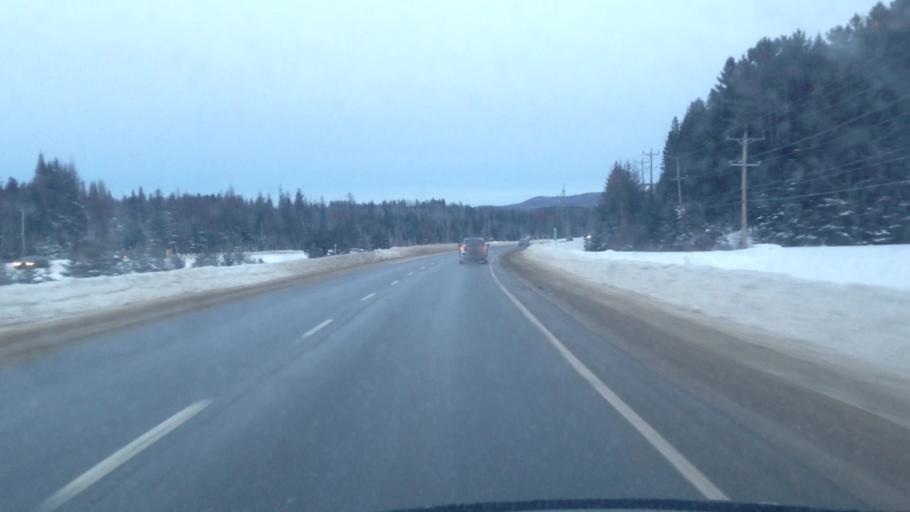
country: CA
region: Quebec
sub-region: Laurentides
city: Mont-Tremblant
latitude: 46.1170
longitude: -74.5570
